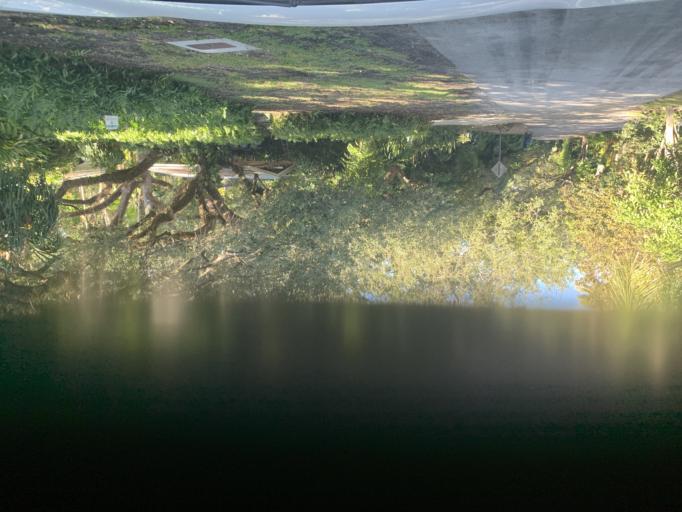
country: US
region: Florida
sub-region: Miami-Dade County
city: Coconut Grove
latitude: 25.7165
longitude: -80.2571
